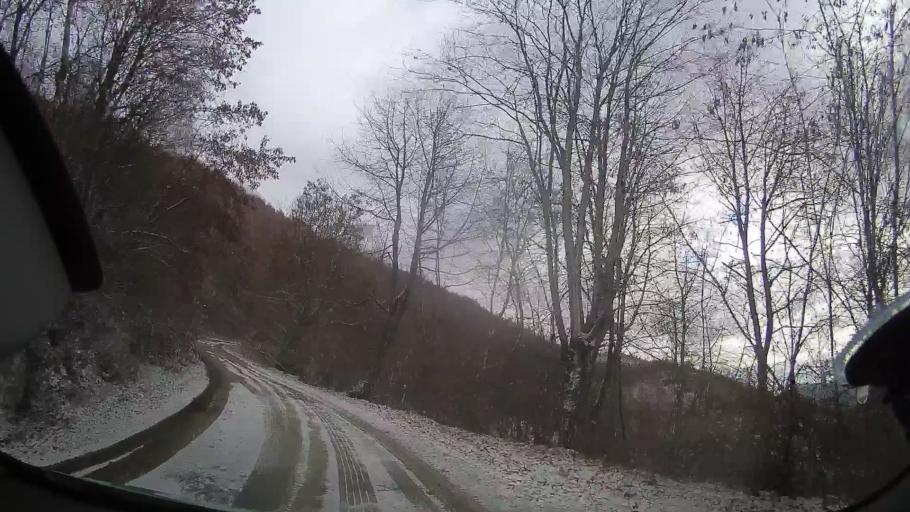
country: RO
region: Cluj
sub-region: Comuna Valea Ierii
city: Valea Ierii
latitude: 46.6520
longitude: 23.3494
